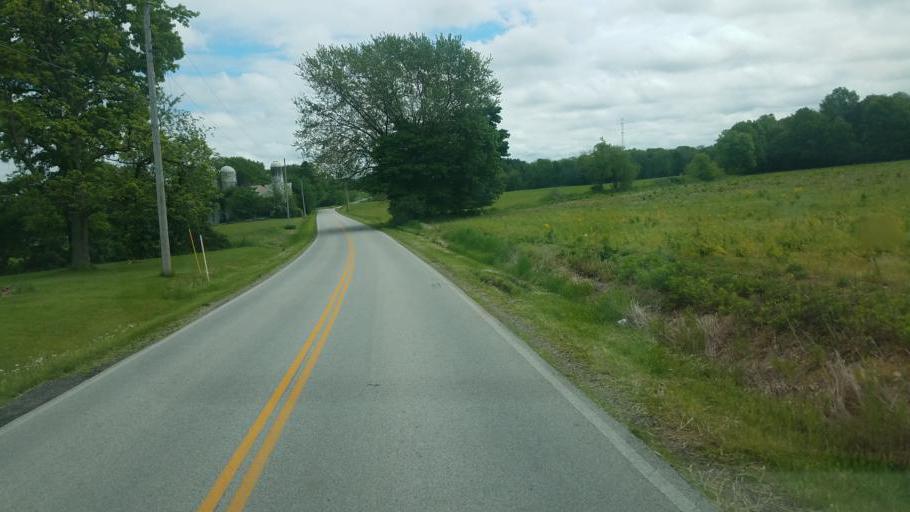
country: US
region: Ohio
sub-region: Wayne County
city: Orrville
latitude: 40.8641
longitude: -81.7788
